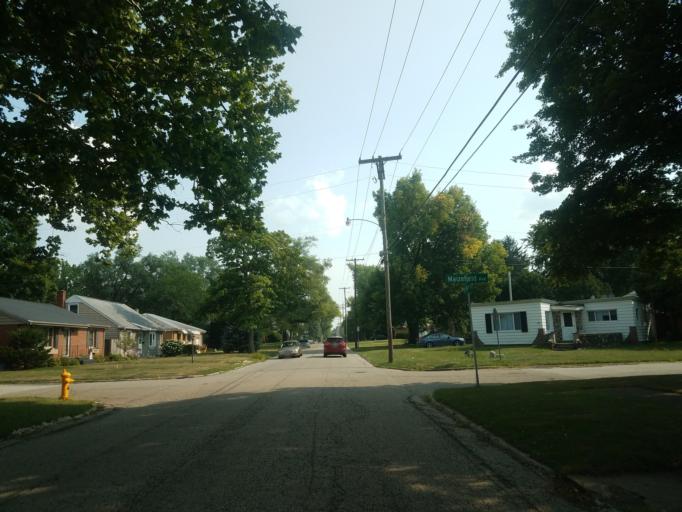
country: US
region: Illinois
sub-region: McLean County
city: Bloomington
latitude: 40.4722
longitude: -88.9724
